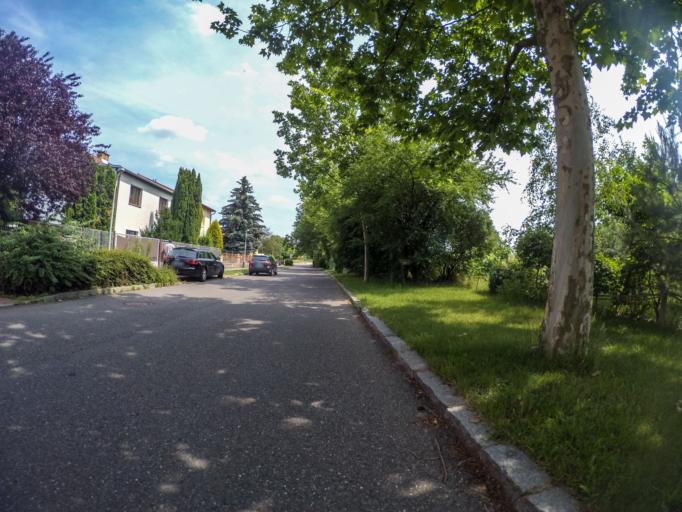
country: CZ
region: Praha
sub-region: Praha 19
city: Kbely
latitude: 50.1276
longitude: 14.5573
